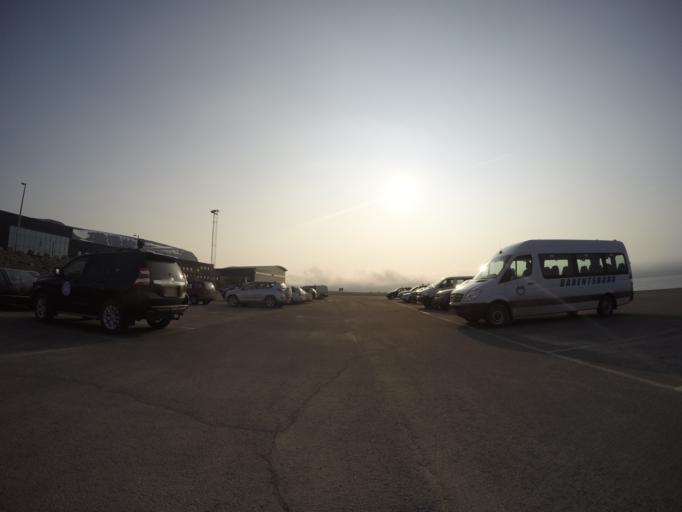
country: SJ
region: Svalbard
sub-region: Spitsbergen
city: Longyearbyen
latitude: 78.2474
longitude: 15.4912
